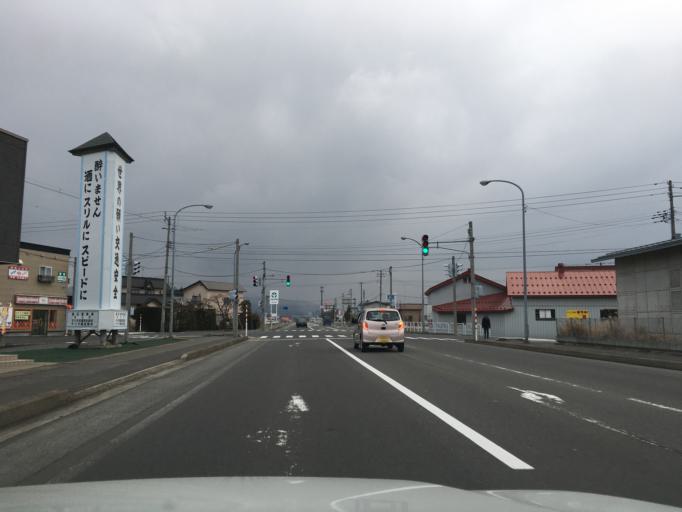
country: JP
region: Aomori
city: Kuroishi
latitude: 40.5847
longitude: 140.5688
